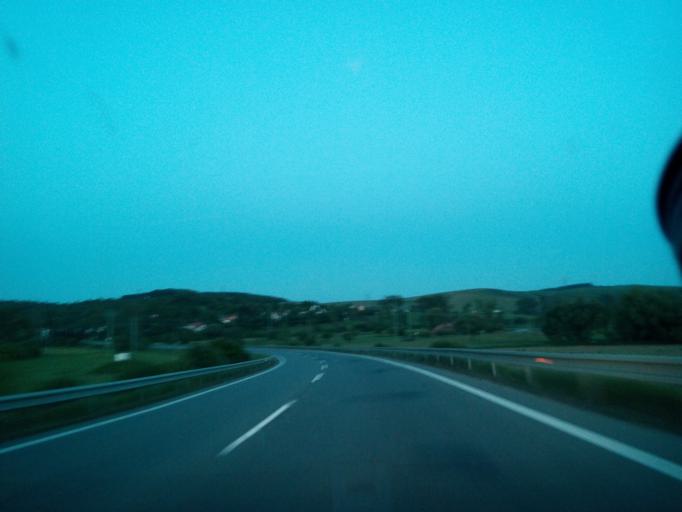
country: SK
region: Banskobystricky
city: Rimavska Sobota
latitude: 48.3884
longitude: 20.0443
